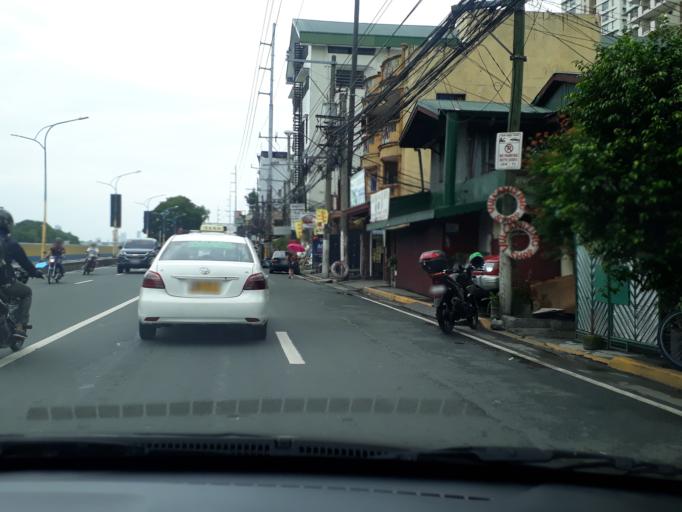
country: PH
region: Metro Manila
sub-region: Mandaluyong
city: Mandaluyong City
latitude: 14.5709
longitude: 121.0310
